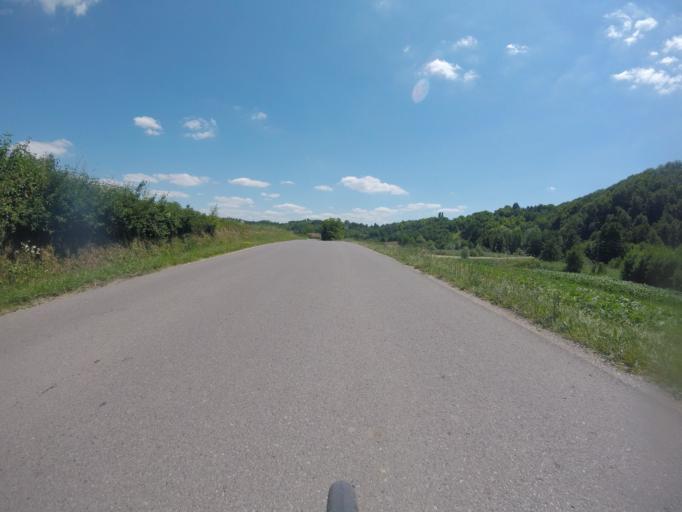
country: HR
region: Karlovacka
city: Ozalj
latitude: 45.6612
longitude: 15.4962
